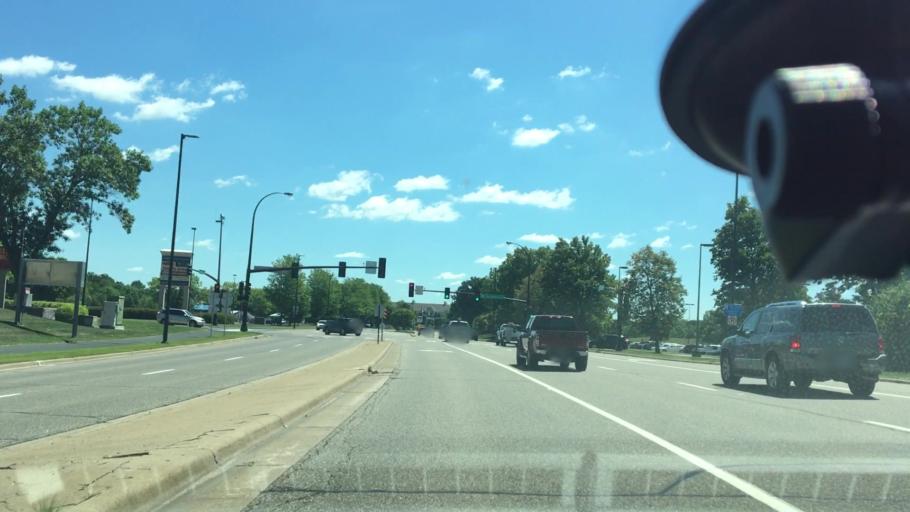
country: US
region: Minnesota
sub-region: Hennepin County
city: Maple Grove
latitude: 45.0657
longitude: -93.4451
